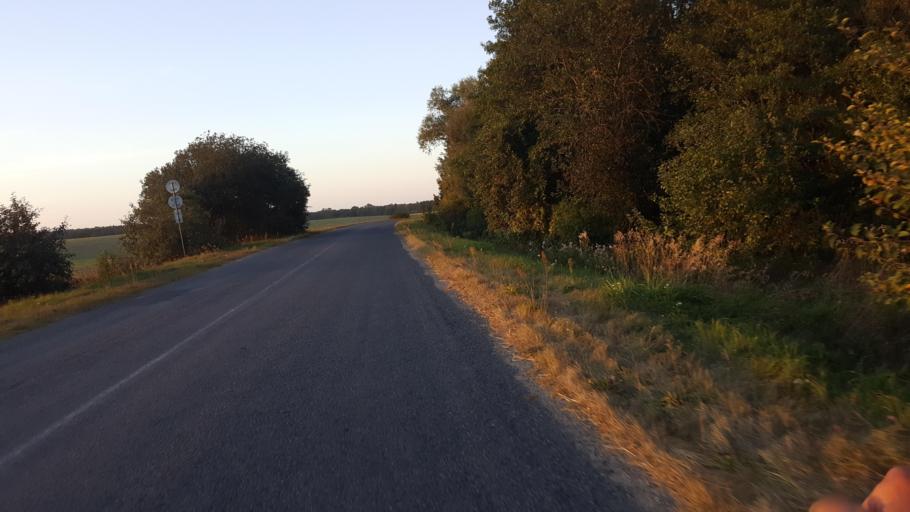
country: BY
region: Brest
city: Charnawchytsy
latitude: 52.3141
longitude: 23.6079
